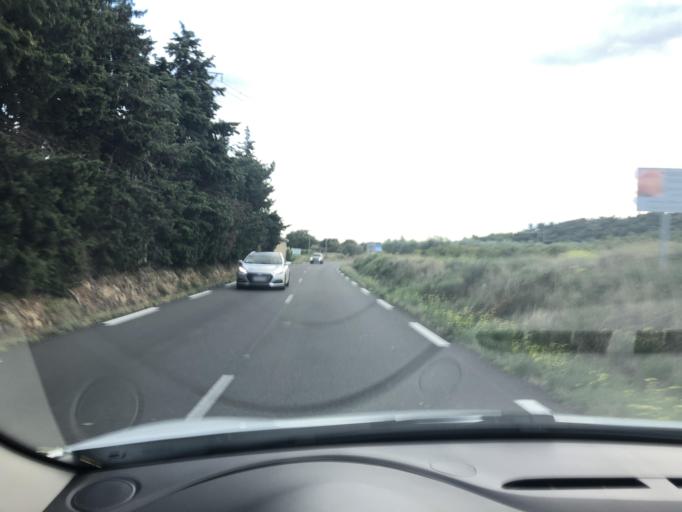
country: FR
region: Provence-Alpes-Cote d'Azur
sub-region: Departement du Vaucluse
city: Caromb
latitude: 44.1118
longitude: 5.0800
